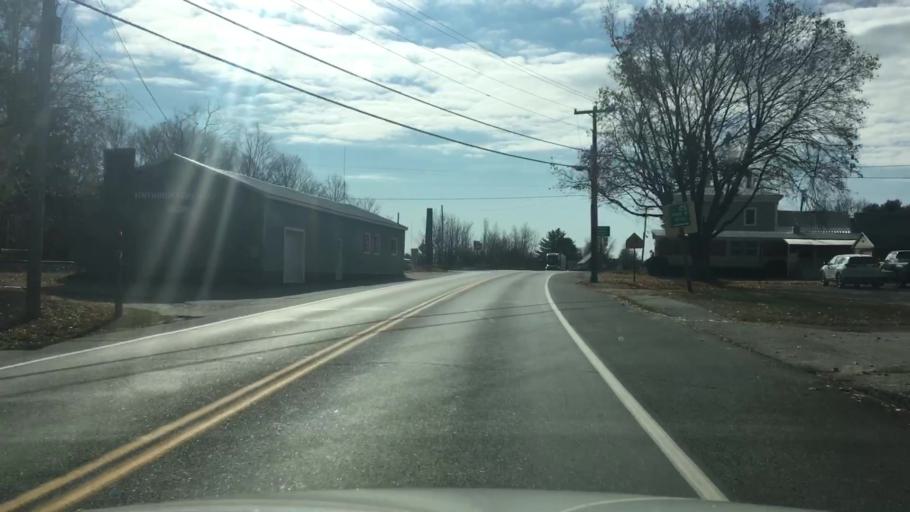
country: US
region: Maine
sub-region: Kennebec County
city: Winthrop
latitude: 44.3061
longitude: -69.9771
